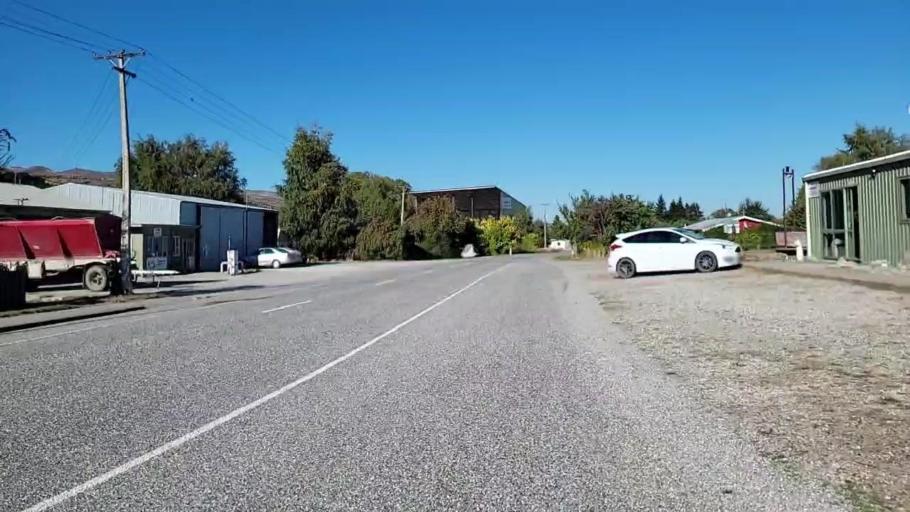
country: NZ
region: Otago
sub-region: Queenstown-Lakes District
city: Wanaka
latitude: -45.0073
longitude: 169.9126
